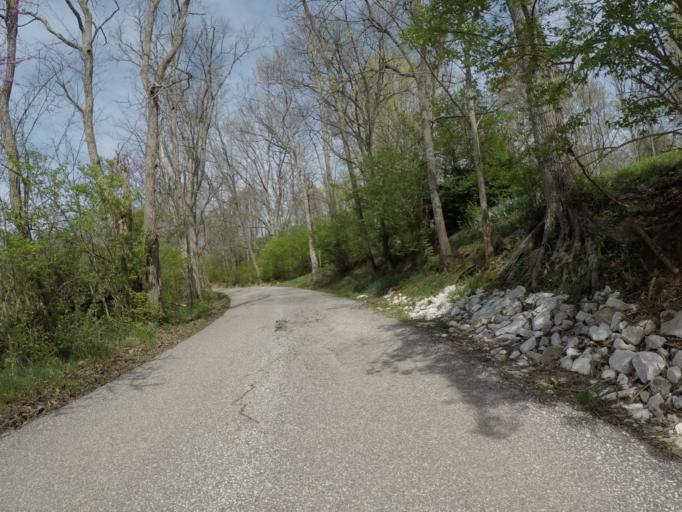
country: US
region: West Virginia
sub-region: Wayne County
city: Lavalette
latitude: 38.3430
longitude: -82.3722
